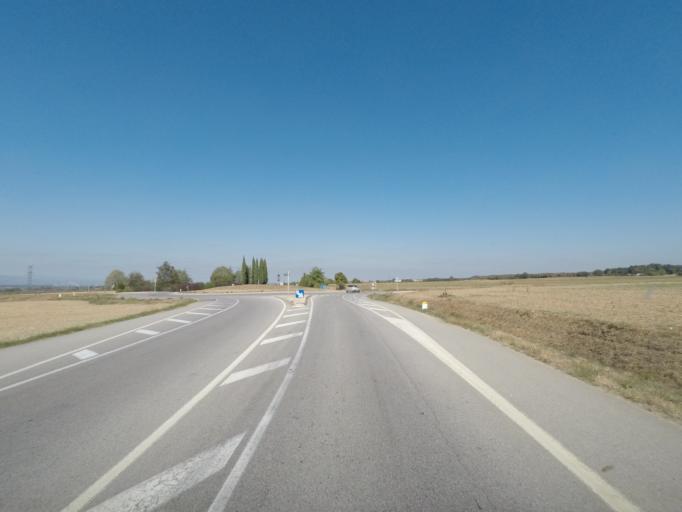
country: FR
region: Rhone-Alpes
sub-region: Departement de la Drome
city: Montmeyran
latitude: 44.8416
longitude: 5.0094
